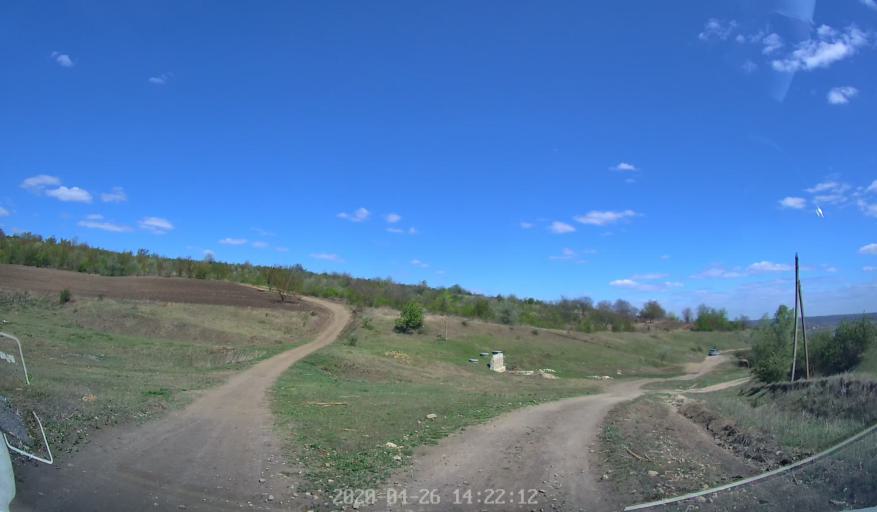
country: MD
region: Telenesti
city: Cocieri
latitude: 47.3602
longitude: 29.0620
